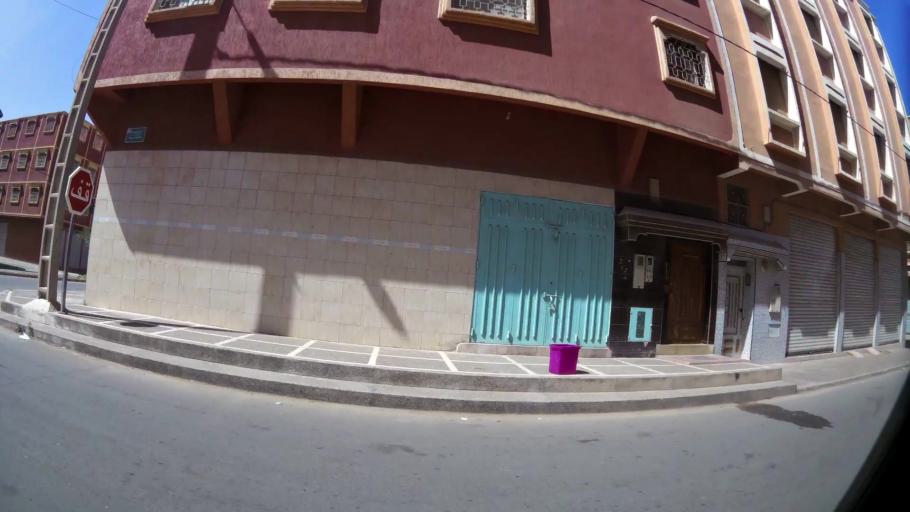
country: MA
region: Souss-Massa-Draa
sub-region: Inezgane-Ait Mellou
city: Inezgane
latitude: 30.3331
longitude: -9.5064
